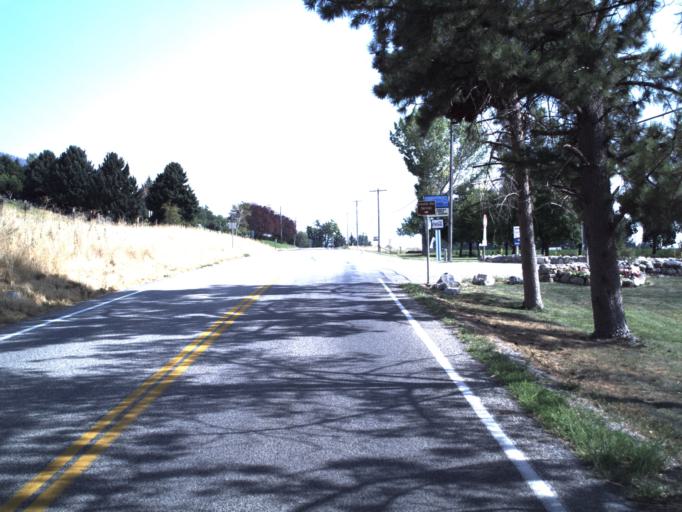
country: US
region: Utah
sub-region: Box Elder County
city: Honeyville
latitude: 41.6590
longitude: -112.0865
